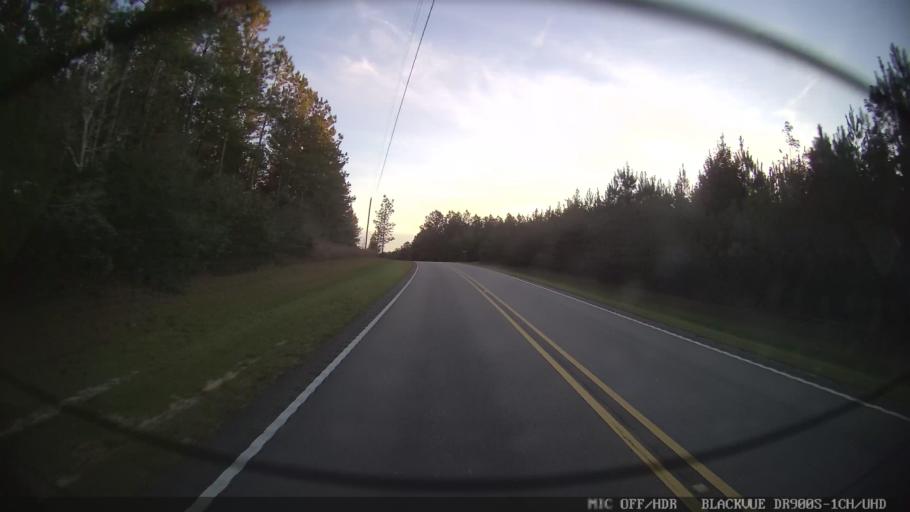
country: US
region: Mississippi
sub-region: Lamar County
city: Lumberton
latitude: 31.0191
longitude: -89.2540
